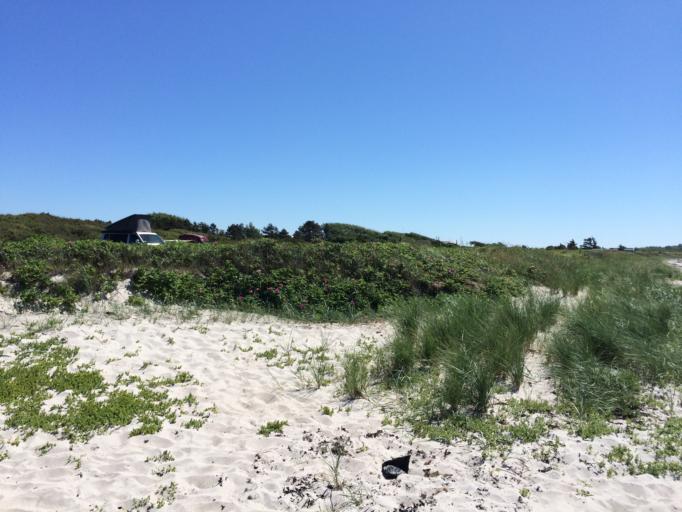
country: DK
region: Central Jutland
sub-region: Samso Kommune
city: Tranebjerg
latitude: 55.9067
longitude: 10.6008
